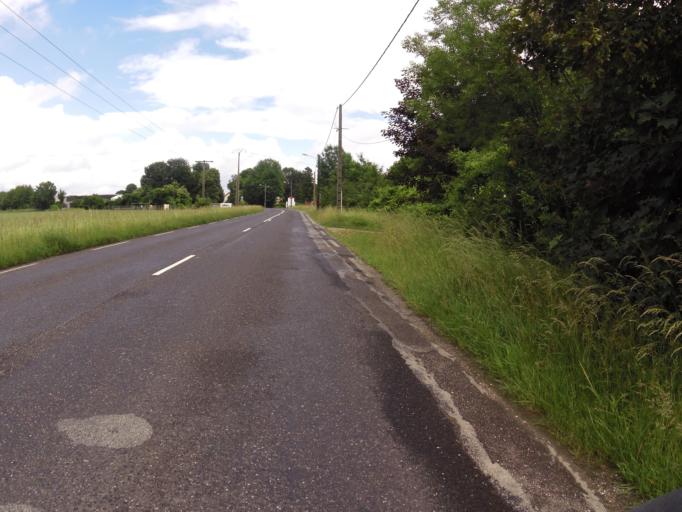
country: FR
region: Lorraine
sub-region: Departement de la Meuse
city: Revigny-sur-Ornain
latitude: 48.8157
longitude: 4.9759
